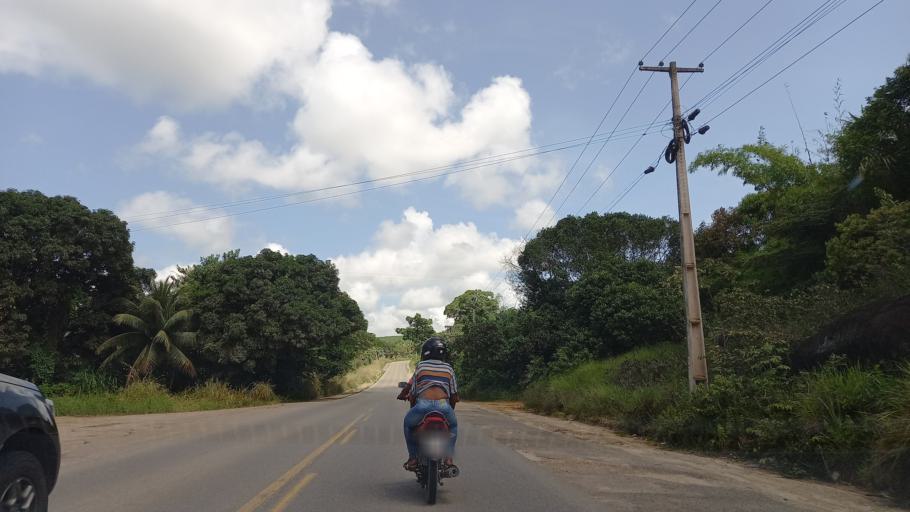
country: BR
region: Pernambuco
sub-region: Sirinhaem
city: Sirinhaem
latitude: -8.6147
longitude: -35.1200
